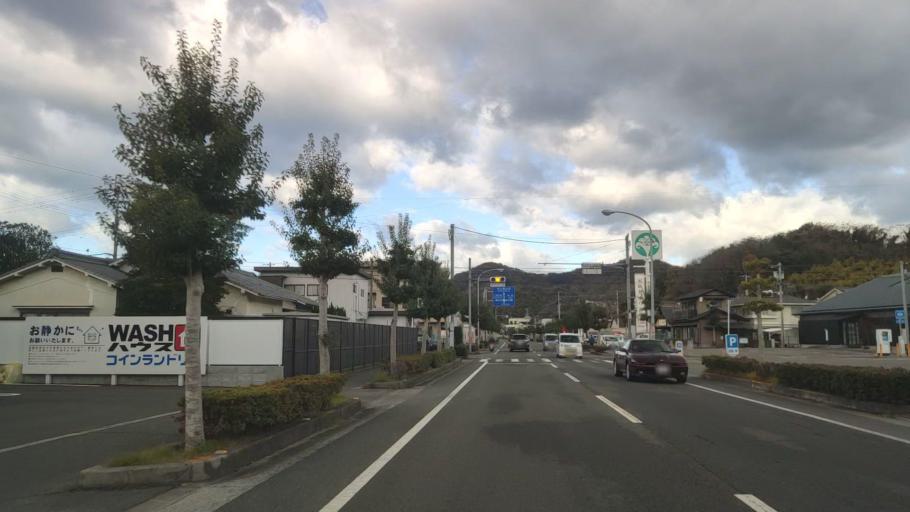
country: JP
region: Ehime
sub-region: Shikoku-chuo Shi
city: Matsuyama
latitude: 33.8697
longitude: 132.7226
